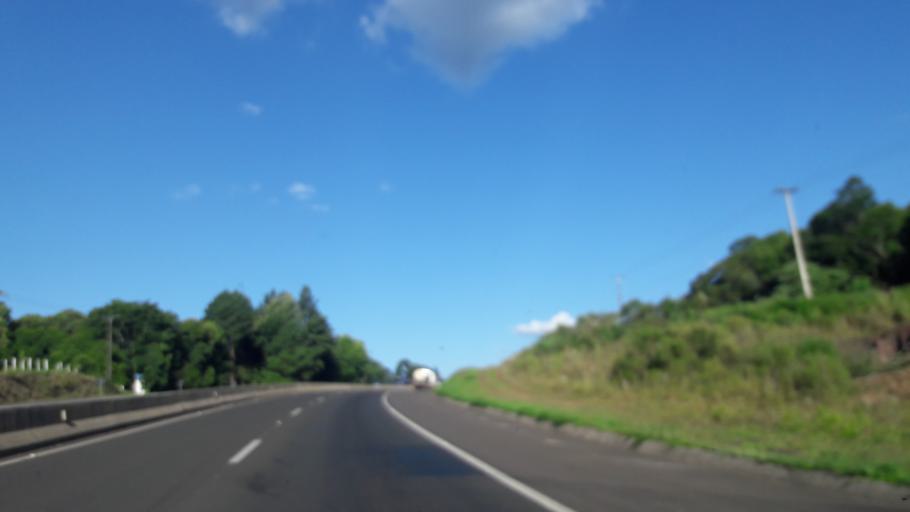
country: BR
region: Parana
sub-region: Guarapuava
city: Guarapuava
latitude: -25.3448
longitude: -51.4019
